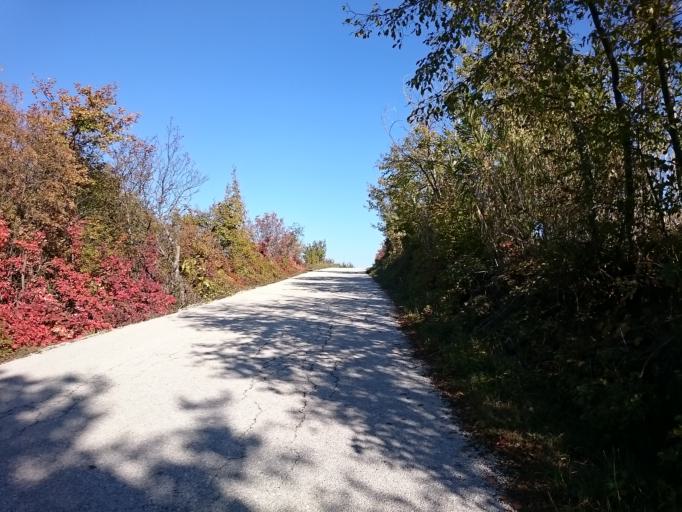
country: HR
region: Istarska
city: Buje
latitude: 45.4354
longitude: 13.7263
